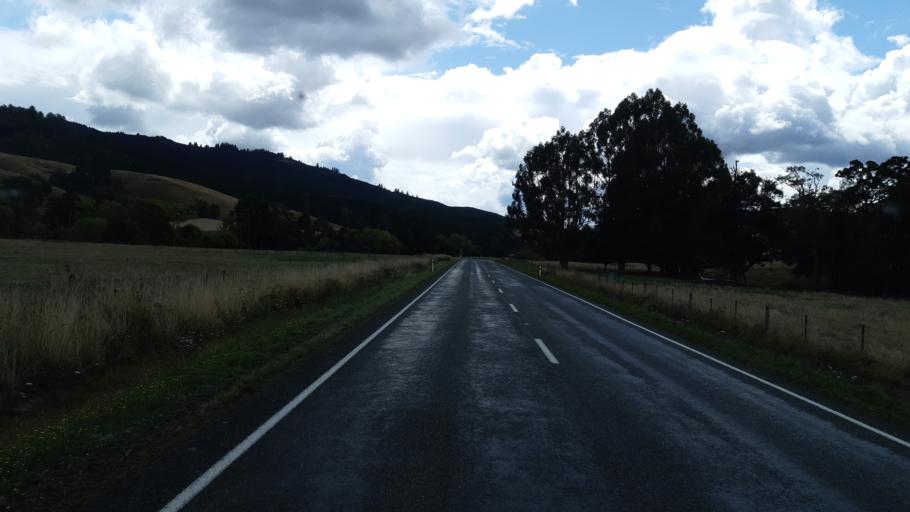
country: NZ
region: Tasman
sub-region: Tasman District
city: Wakefield
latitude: -41.5660
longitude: 172.7777
